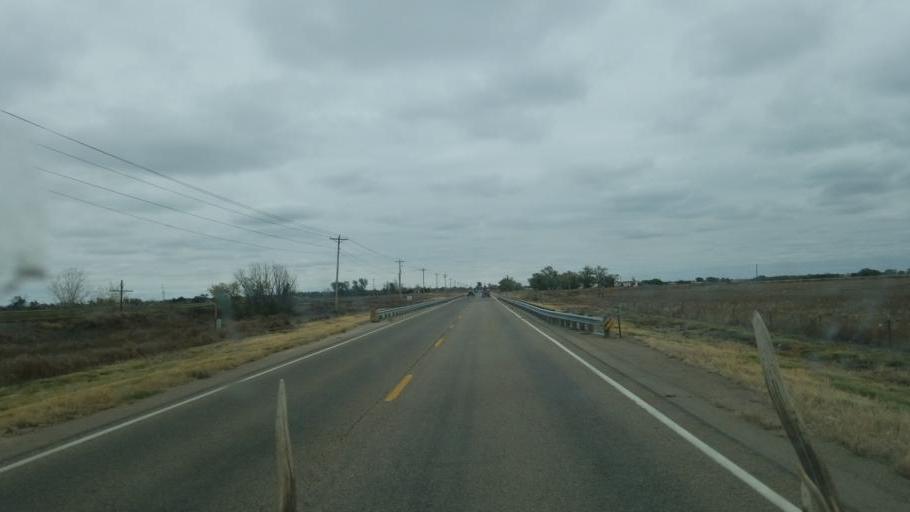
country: US
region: Colorado
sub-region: Crowley County
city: Ordway
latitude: 38.2085
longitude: -103.7892
